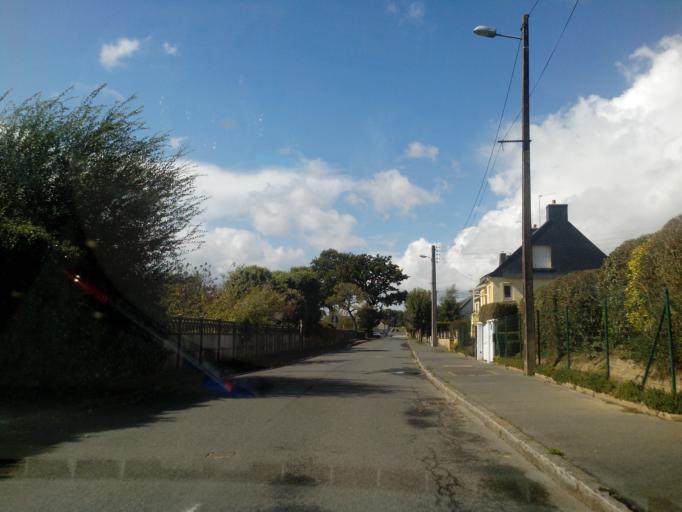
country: FR
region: Brittany
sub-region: Departement des Cotes-d'Armor
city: Merdrignac
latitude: 48.1918
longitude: -2.4176
